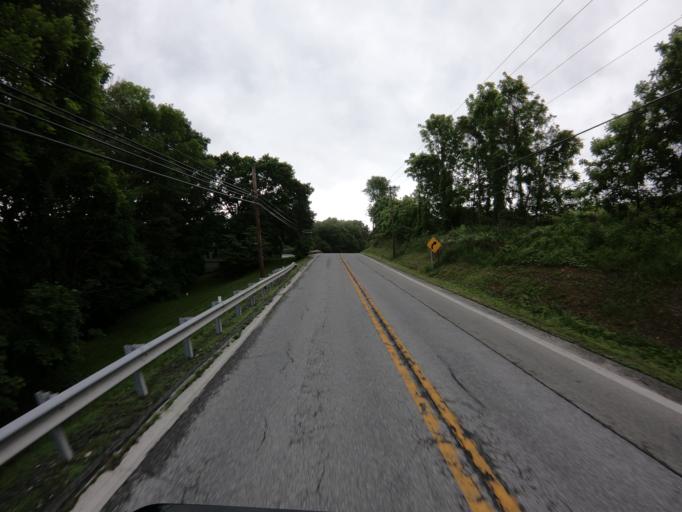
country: US
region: Maryland
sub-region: Frederick County
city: Middletown
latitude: 39.4558
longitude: -77.5726
